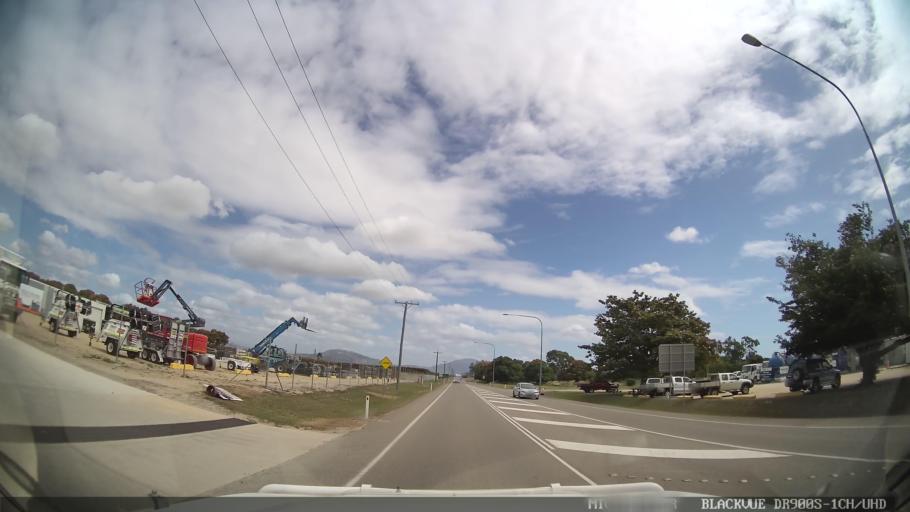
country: AU
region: Queensland
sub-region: Whitsunday
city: Bowen
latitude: -20.0164
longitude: 148.1892
